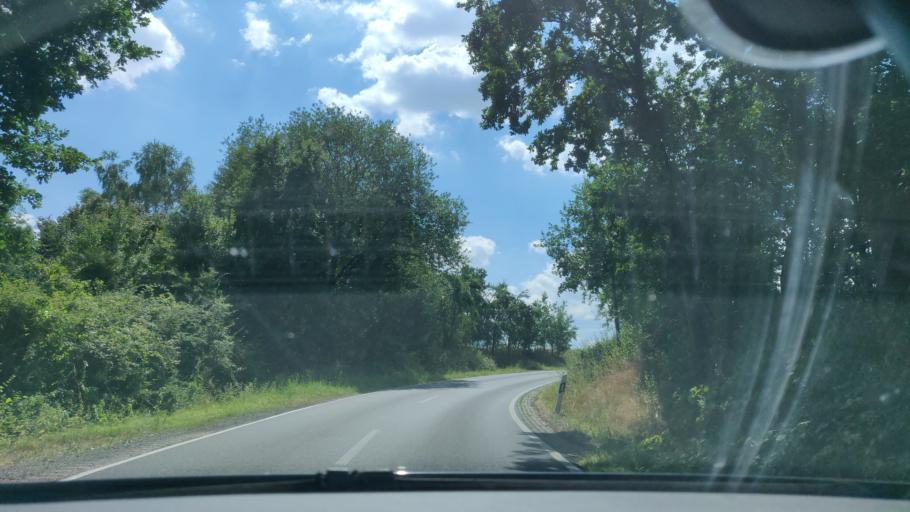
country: DE
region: Hesse
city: Gudensberg
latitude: 51.1567
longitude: 9.3460
